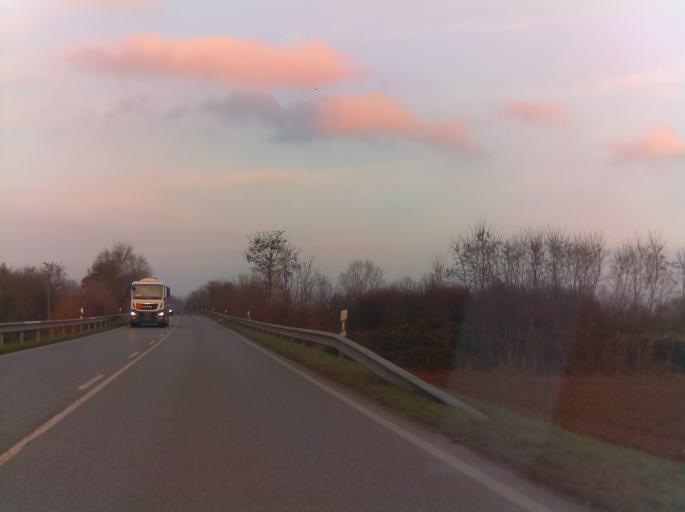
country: DE
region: Baden-Wuerttemberg
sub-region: Karlsruhe Region
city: Leimen
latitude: 49.3582
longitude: 8.6746
